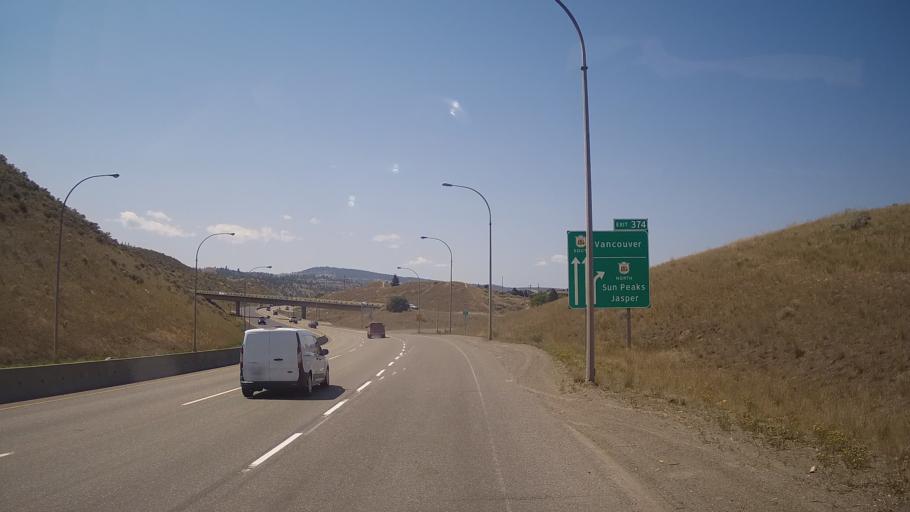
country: CA
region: British Columbia
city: Kamloops
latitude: 50.6717
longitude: -120.3004
